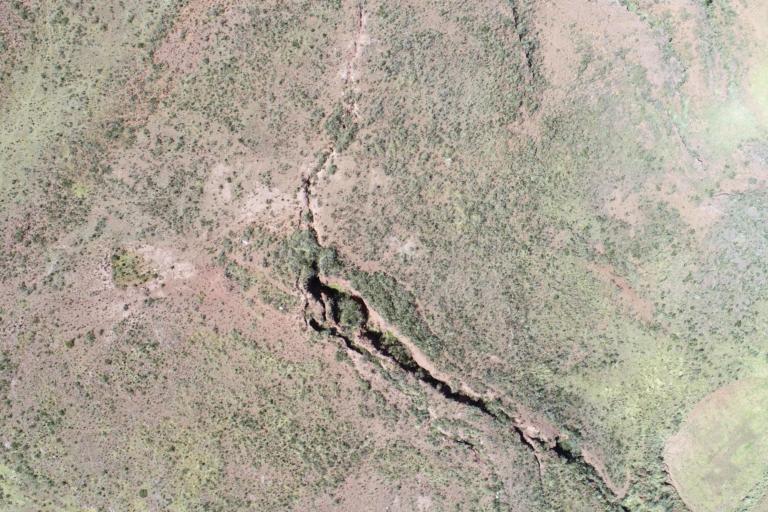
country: BO
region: La Paz
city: Tiahuanaco
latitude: -16.5955
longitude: -68.7591
